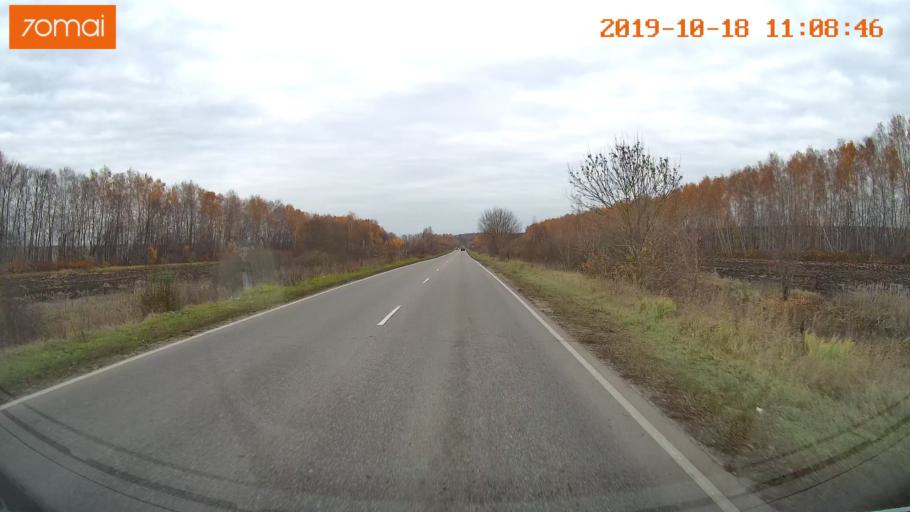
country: RU
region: Tula
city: Kimovsk
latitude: 53.9432
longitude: 38.5352
